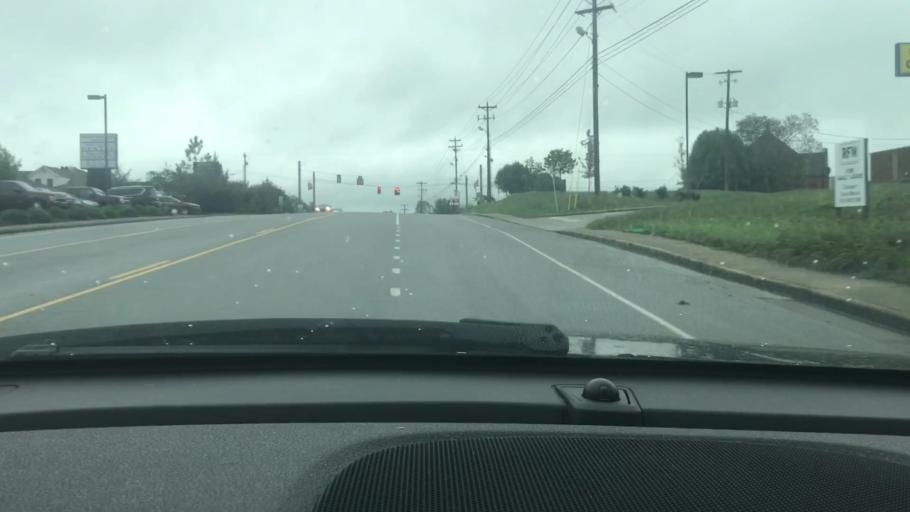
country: US
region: Tennessee
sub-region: Cheatham County
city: Kingston Springs
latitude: 36.0875
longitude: -87.1025
